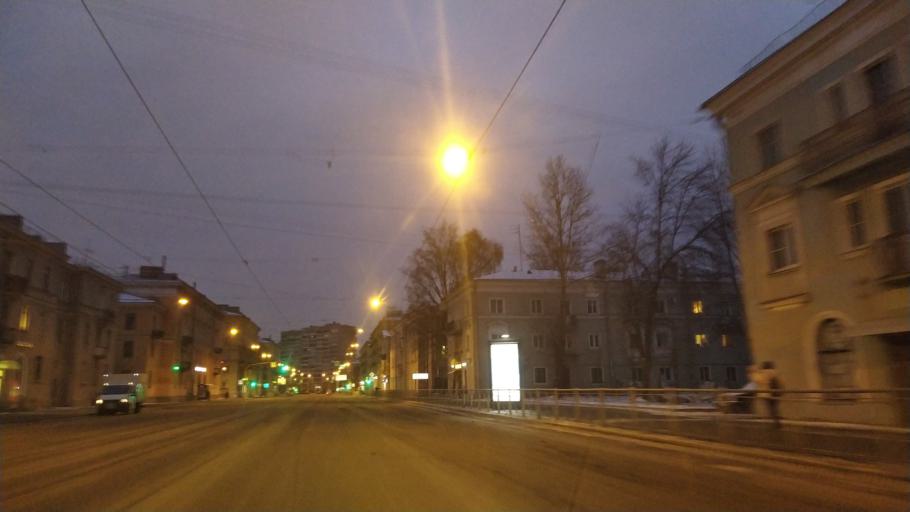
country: RU
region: Leningrad
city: Kalininskiy
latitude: 59.9562
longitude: 30.4154
